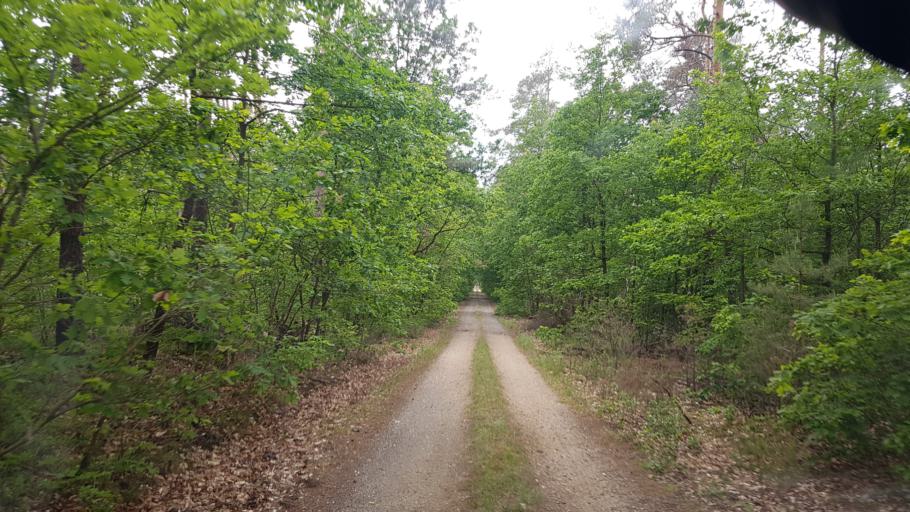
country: DE
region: Brandenburg
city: Hohenleipisch
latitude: 51.5236
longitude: 13.5342
